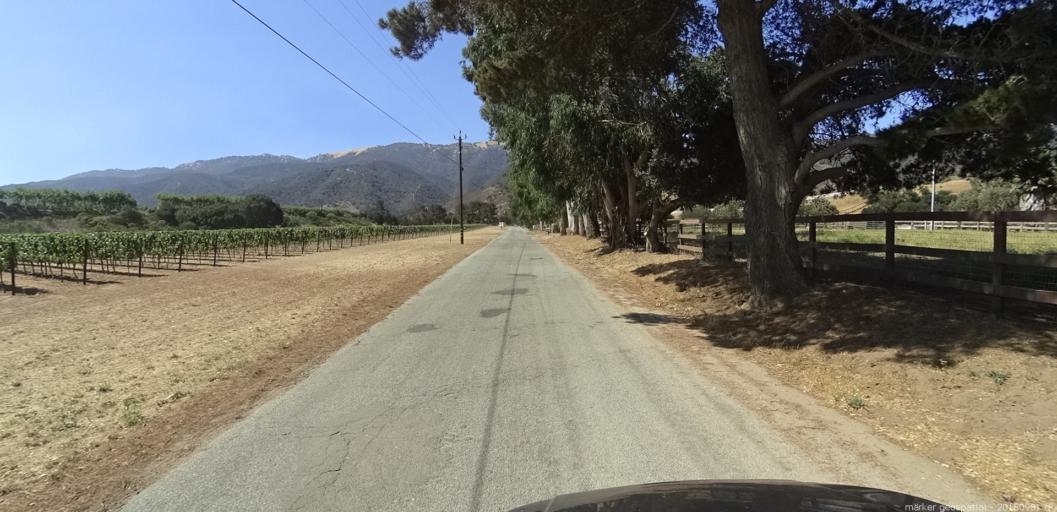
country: US
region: California
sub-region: Monterey County
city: Chualar
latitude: 36.5195
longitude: -121.5234
